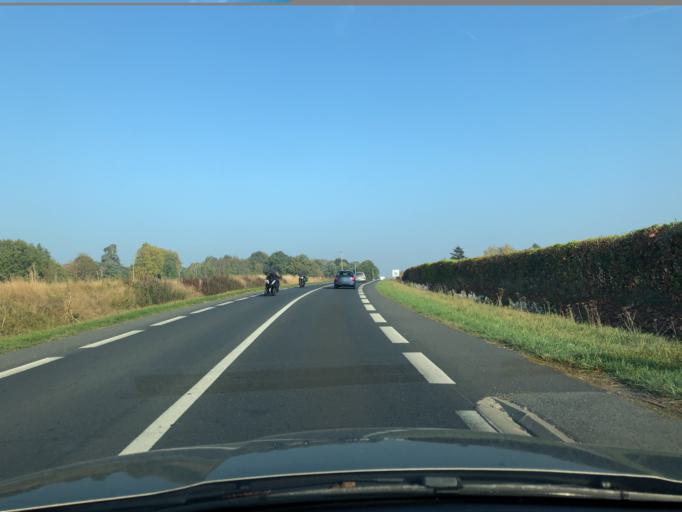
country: FR
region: Centre
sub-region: Departement d'Indre-et-Loire
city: Chanceaux-sur-Choisille
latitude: 47.4457
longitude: 0.6988
